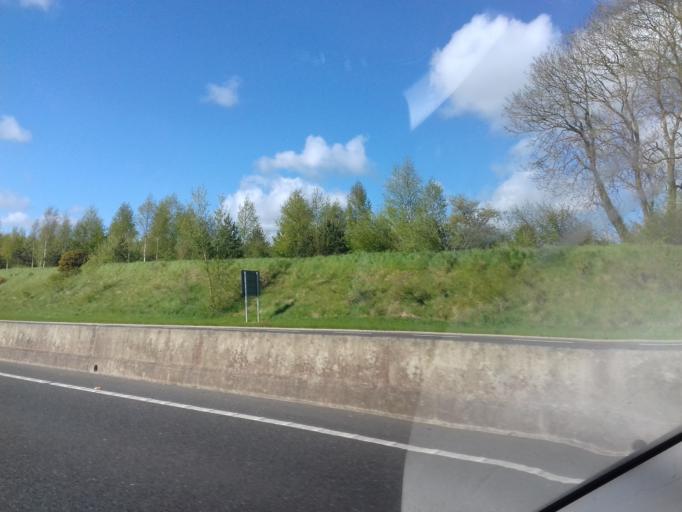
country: IE
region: Munster
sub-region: Waterford
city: Waterford
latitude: 52.3188
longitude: -7.1434
